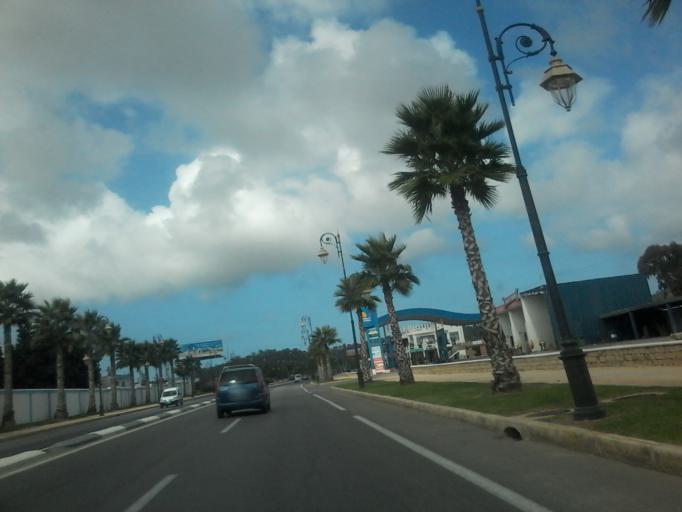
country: MA
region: Tanger-Tetouan
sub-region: Tetouan
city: Martil
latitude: 35.6571
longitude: -5.3190
